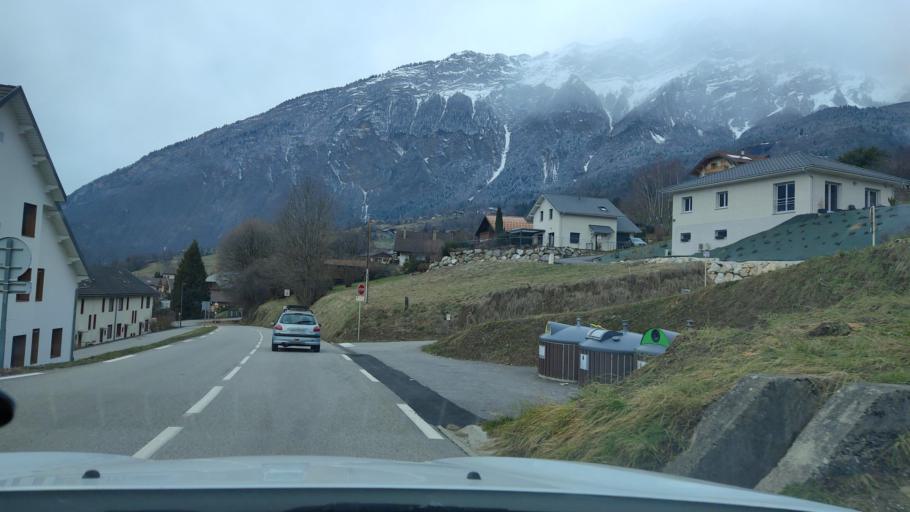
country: FR
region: Rhone-Alpes
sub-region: Departement de la Savoie
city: Ugine
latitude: 45.7578
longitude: 6.4213
